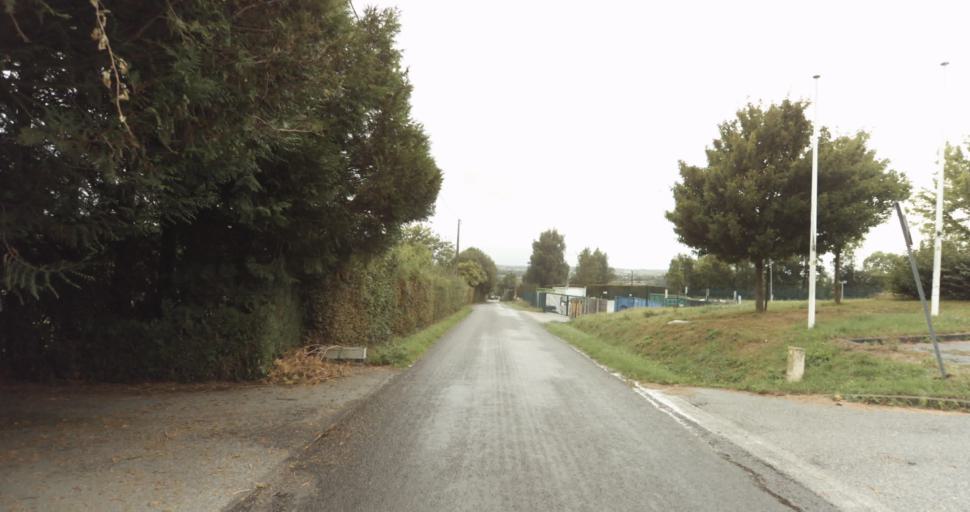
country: FR
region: Lower Normandy
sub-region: Departement de l'Orne
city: Sainte-Gauburge-Sainte-Colombe
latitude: 48.7144
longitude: 0.4383
